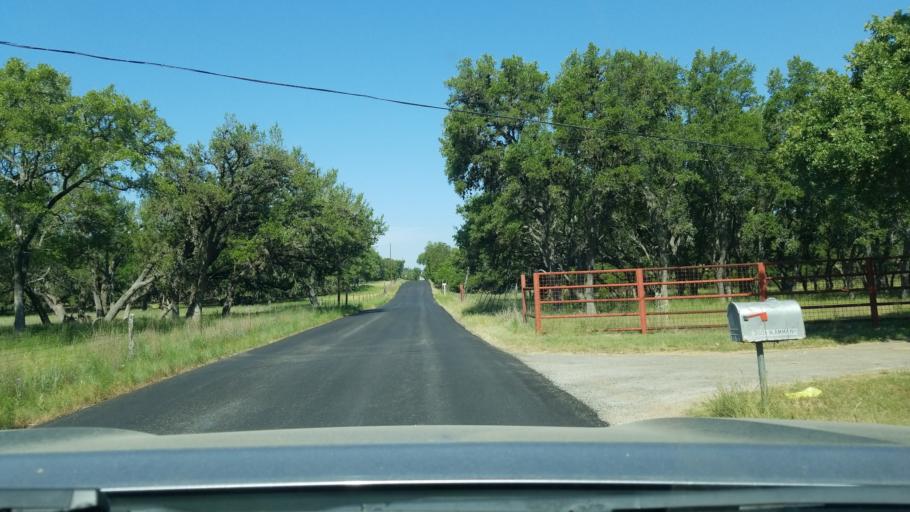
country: US
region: Texas
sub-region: Bexar County
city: Timberwood Park
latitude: 29.7693
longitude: -98.5463
